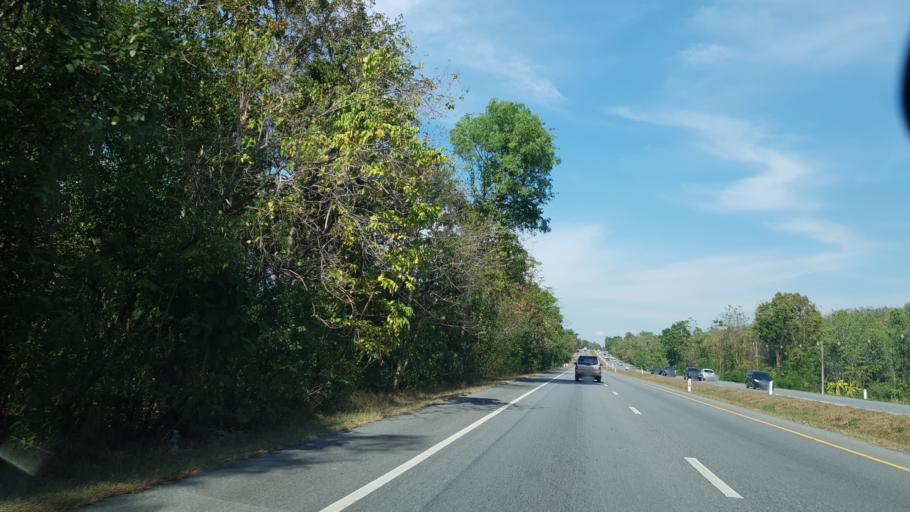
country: TH
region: Uttaradit
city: Thong Saen Khan
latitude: 17.4149
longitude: 100.2278
